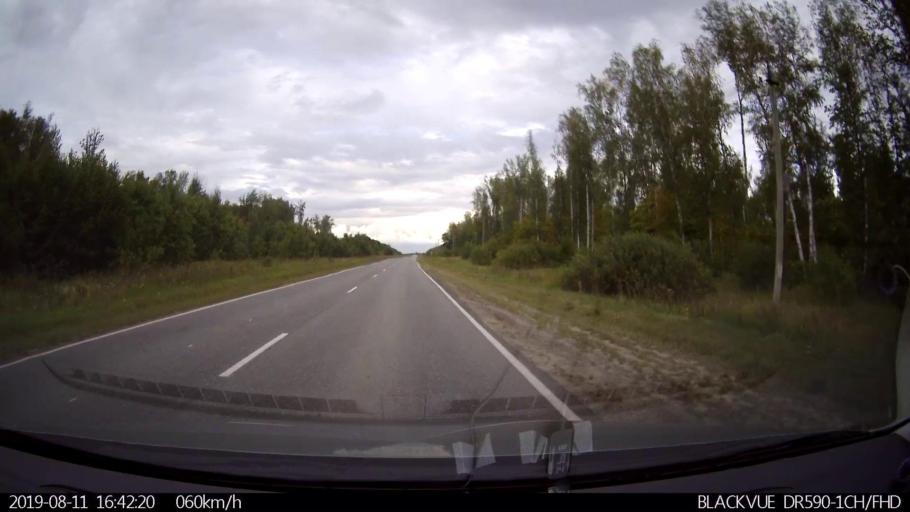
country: RU
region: Ulyanovsk
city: Mayna
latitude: 54.1597
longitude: 47.6614
